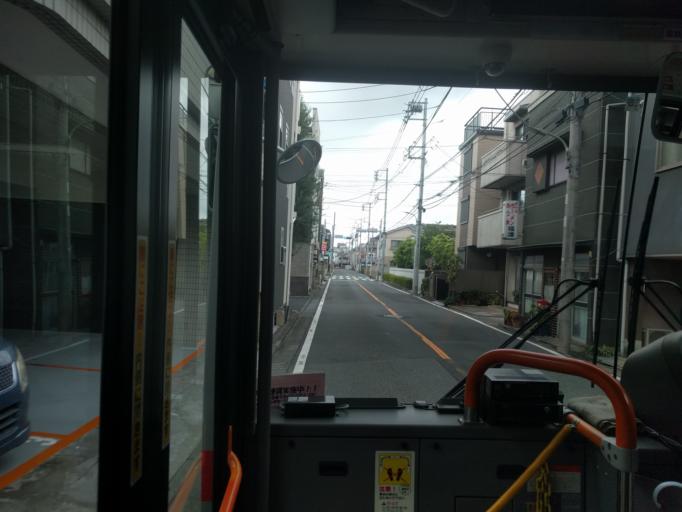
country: JP
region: Kanagawa
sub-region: Kawasaki-shi
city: Kawasaki
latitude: 35.5518
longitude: 139.7213
